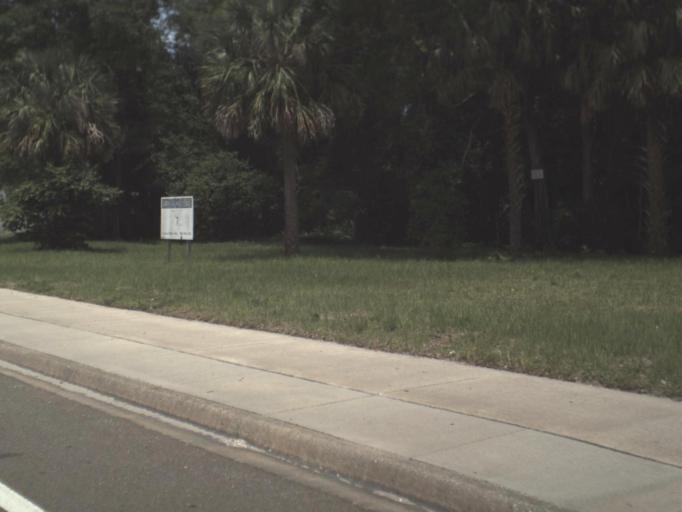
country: US
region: Florida
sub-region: Duval County
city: Jacksonville
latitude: 30.3771
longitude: -81.6510
